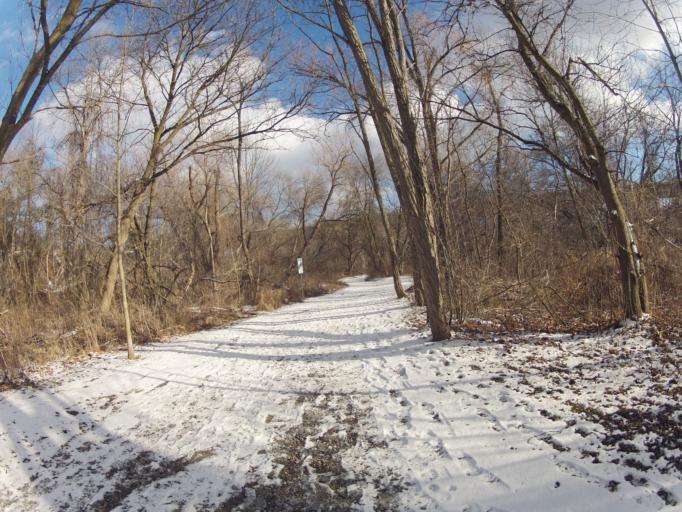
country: CA
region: Ontario
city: Mississauga
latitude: 43.5626
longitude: -79.6734
